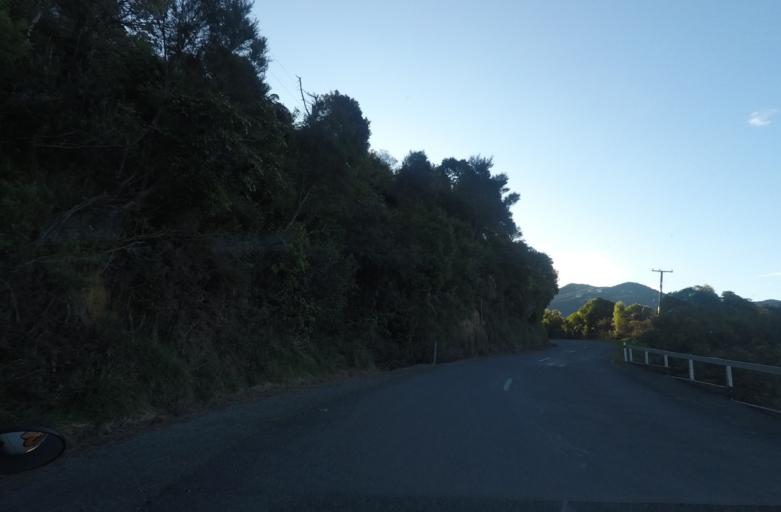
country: NZ
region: Marlborough
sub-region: Marlborough District
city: Picton
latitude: -41.2703
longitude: 173.9583
